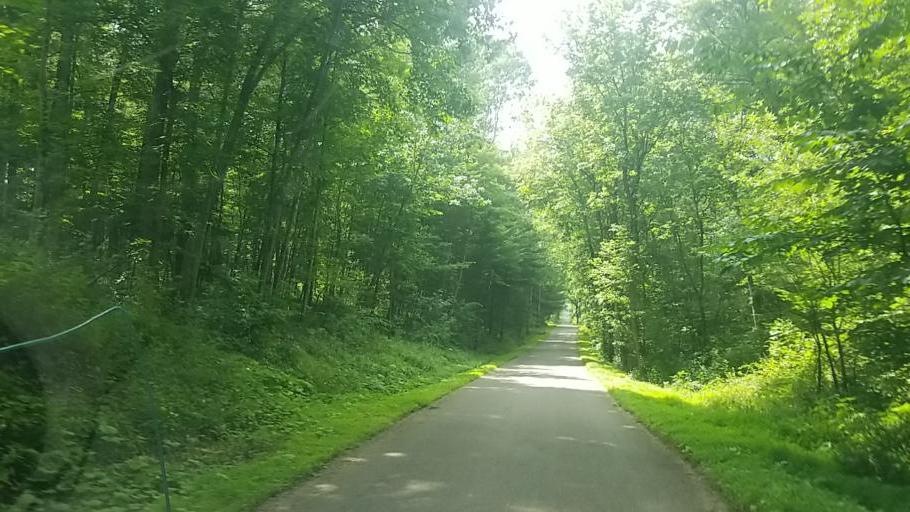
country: US
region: Ohio
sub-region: Knox County
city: Gambier
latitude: 40.2614
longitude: -82.2887
